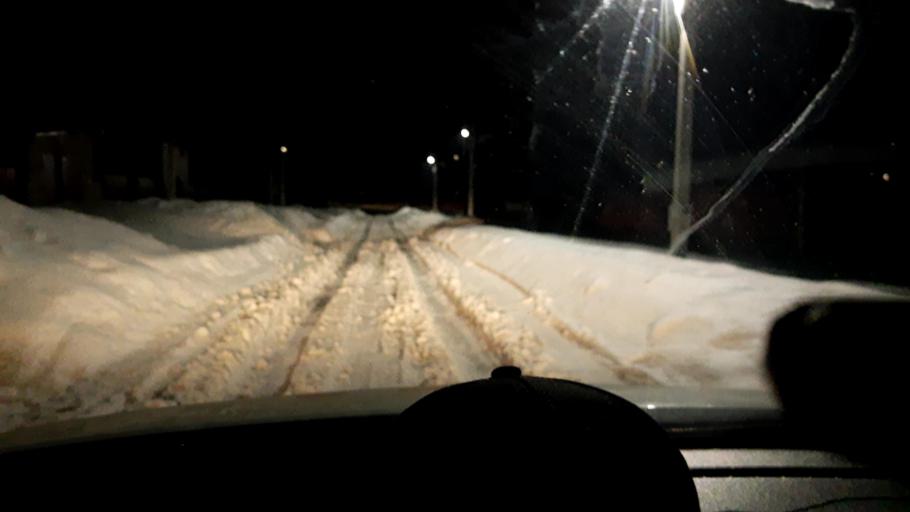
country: RU
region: Bashkortostan
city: Kabakovo
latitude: 54.5931
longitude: 56.2326
